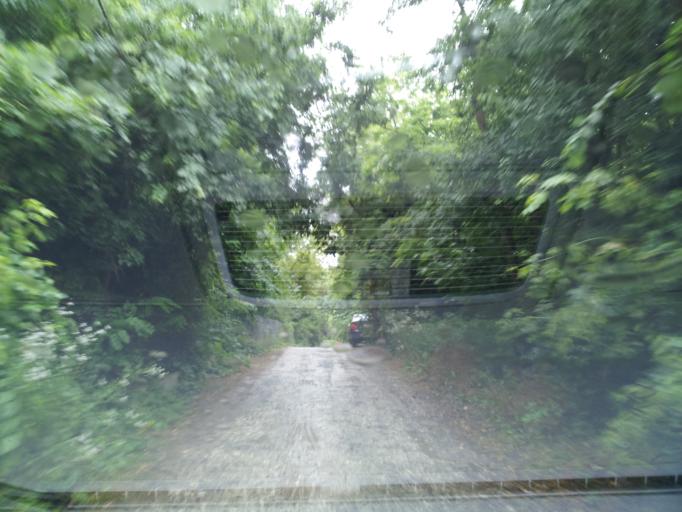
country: HU
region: Fejer
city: Lepseny
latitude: 46.9960
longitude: 18.1686
